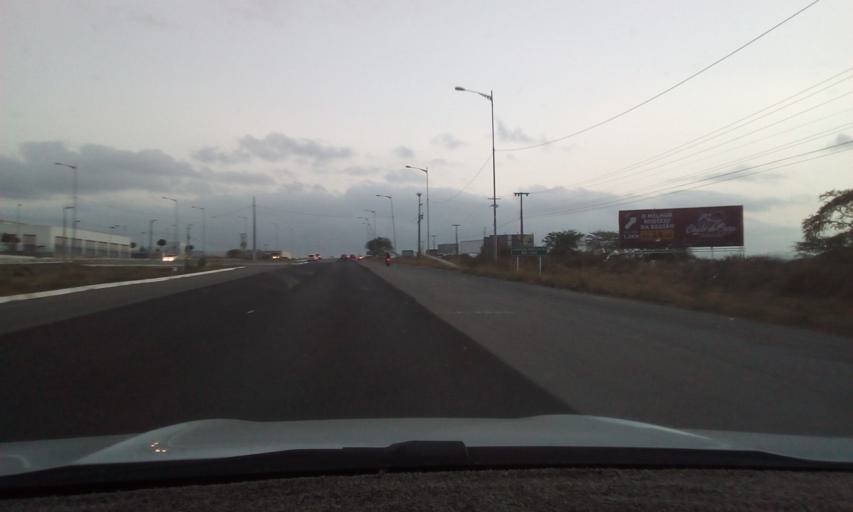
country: BR
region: Pernambuco
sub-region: Caruaru
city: Caruaru
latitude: -8.2447
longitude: -35.9753
